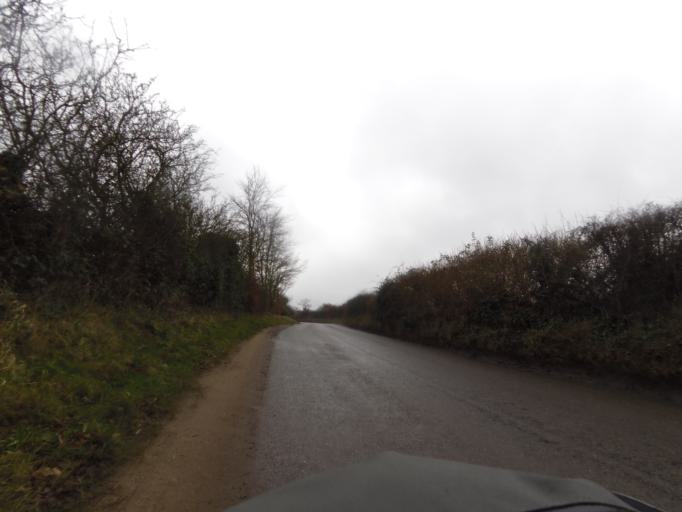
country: GB
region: England
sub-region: Norfolk
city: Briston
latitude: 52.8711
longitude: 1.0751
